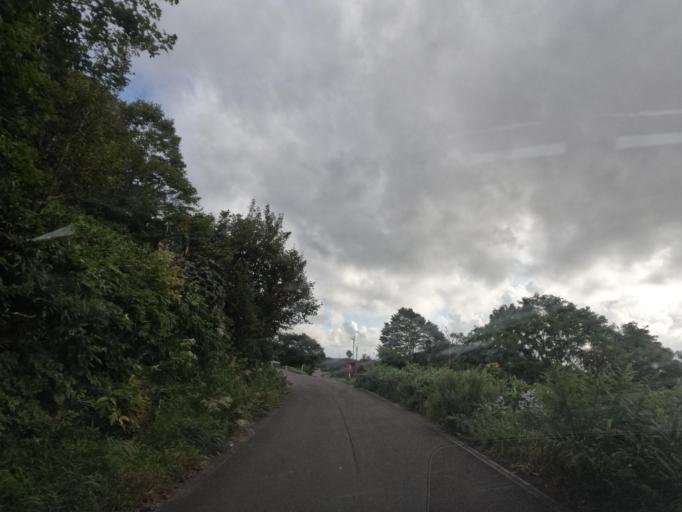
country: JP
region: Hokkaido
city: Muroran
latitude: 42.3206
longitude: 141.0027
